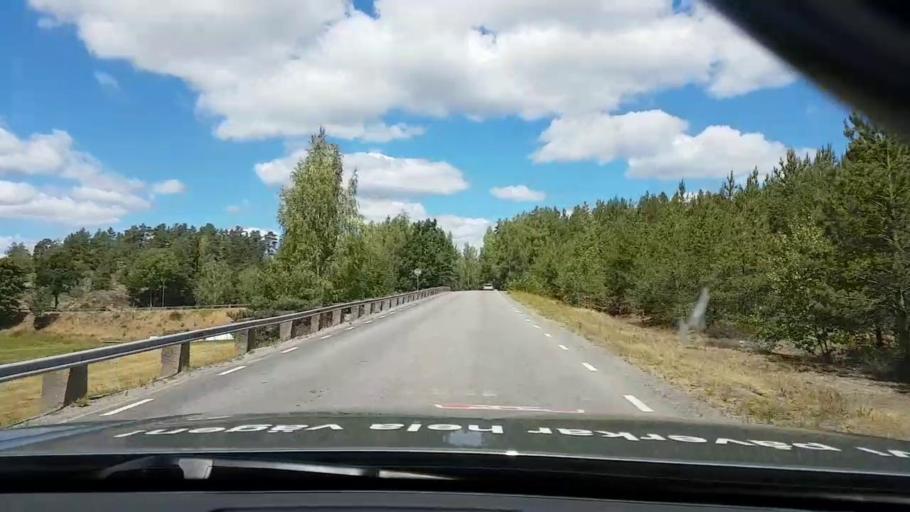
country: SE
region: Kalmar
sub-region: Vasterviks Kommun
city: Forserum
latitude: 58.0238
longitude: 16.5731
